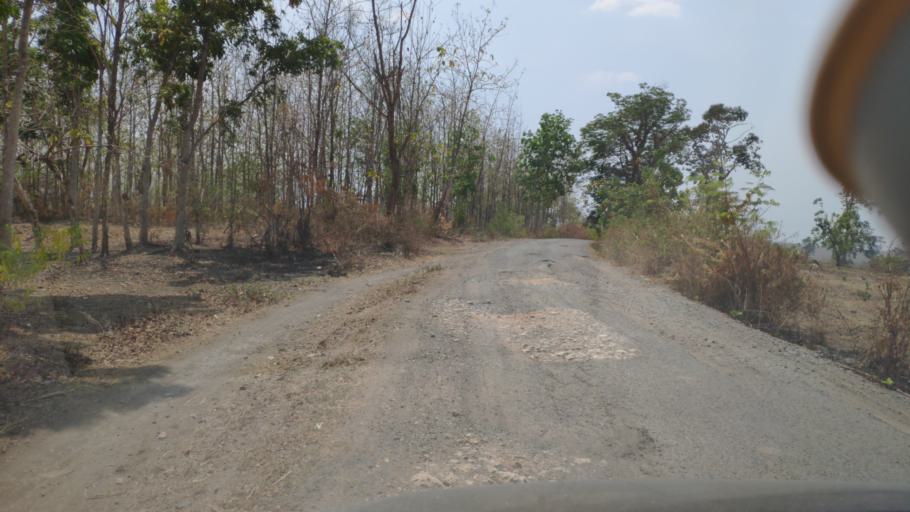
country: ID
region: Central Java
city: Pipes
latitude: -7.1499
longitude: 111.2746
